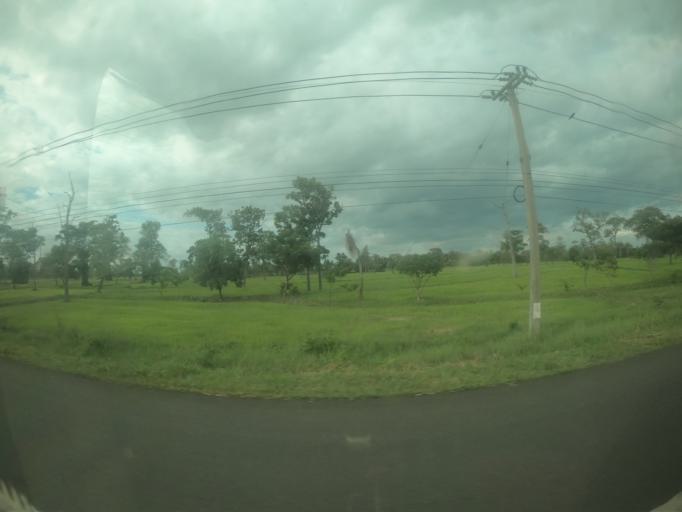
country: TH
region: Surin
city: Kap Choeng
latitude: 14.5388
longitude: 103.5223
